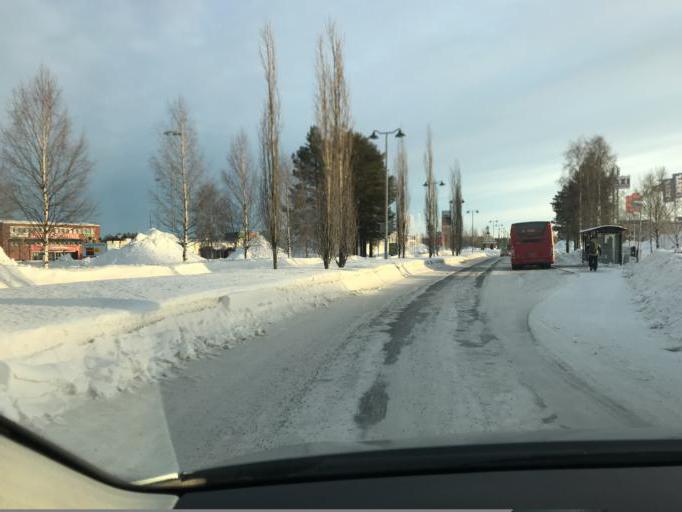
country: SE
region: Norrbotten
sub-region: Lulea Kommun
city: Gammelstad
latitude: 65.6172
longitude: 22.0433
